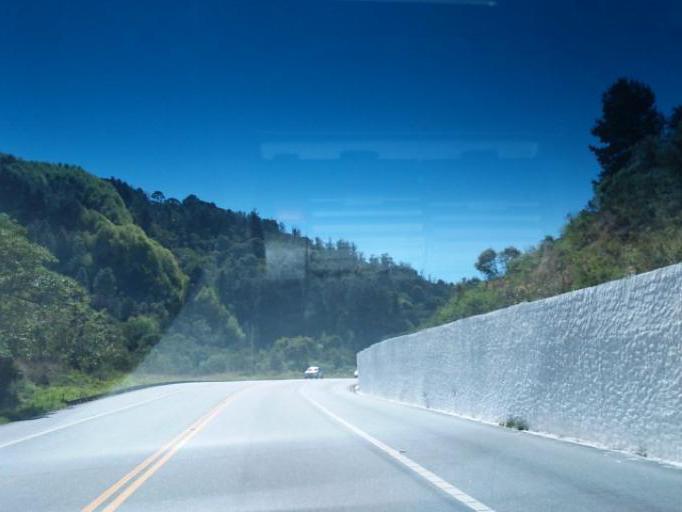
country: BR
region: Sao Paulo
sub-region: Campos Do Jordao
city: Campos do Jordao
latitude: -22.7794
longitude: -45.6109
